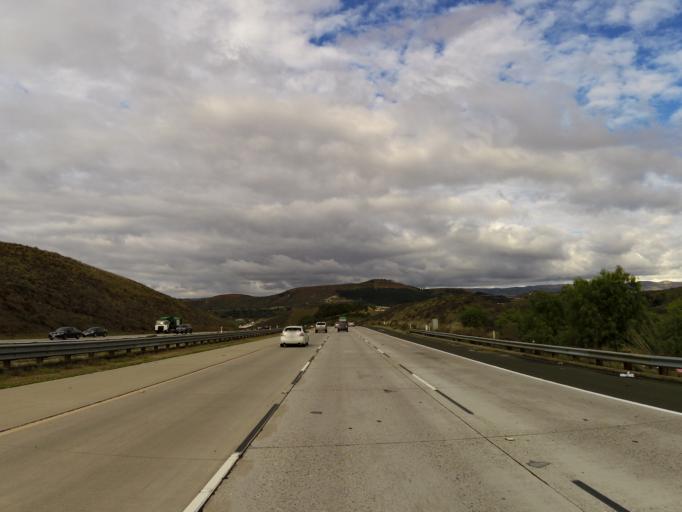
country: US
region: California
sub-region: Ventura County
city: Moorpark
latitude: 34.2524
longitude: -118.8400
